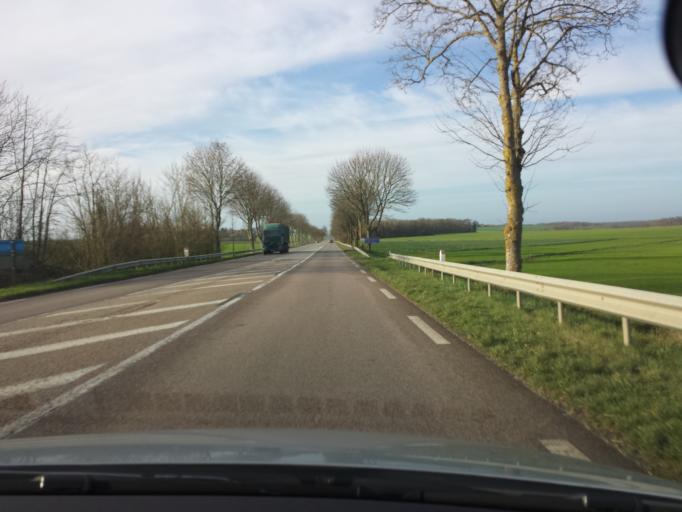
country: FR
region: Haute-Normandie
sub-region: Departement de l'Eure
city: Breuilpont
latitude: 49.0180
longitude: 1.4745
